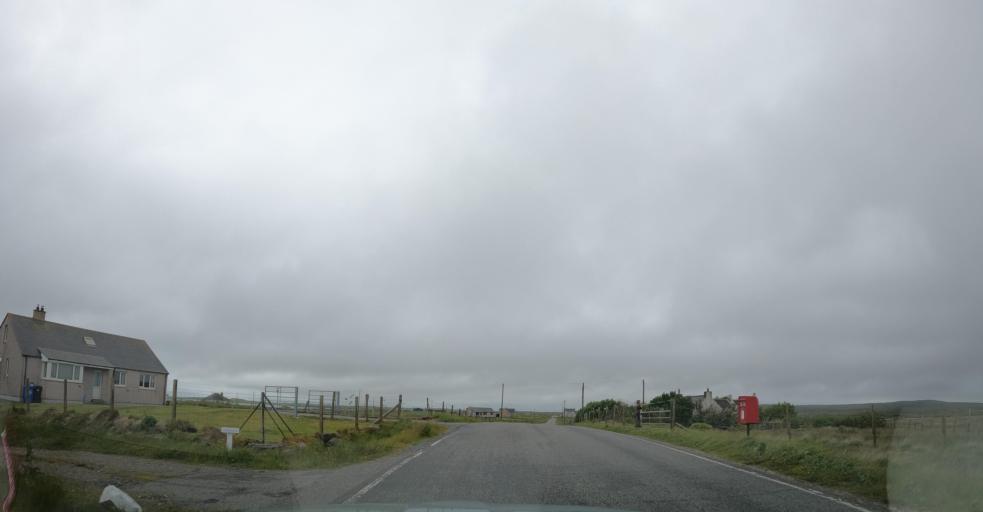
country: GB
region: Scotland
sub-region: Eilean Siar
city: Isle of North Uist
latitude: 57.5717
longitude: -7.3983
